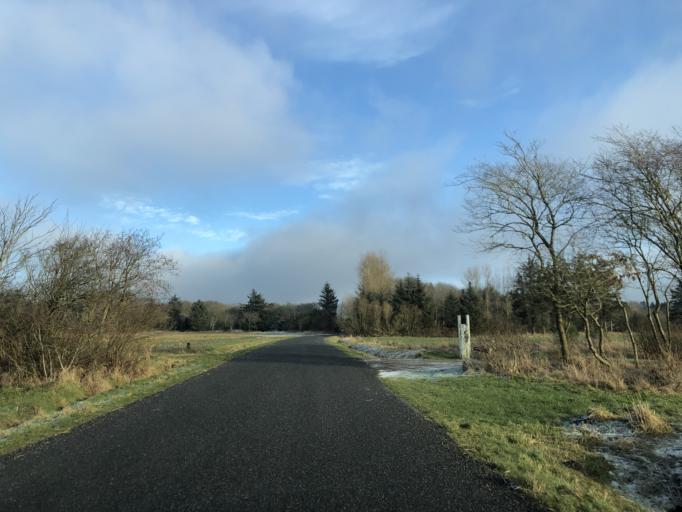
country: DK
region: Central Jutland
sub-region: Holstebro Kommune
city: Ulfborg
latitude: 56.2050
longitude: 8.3343
